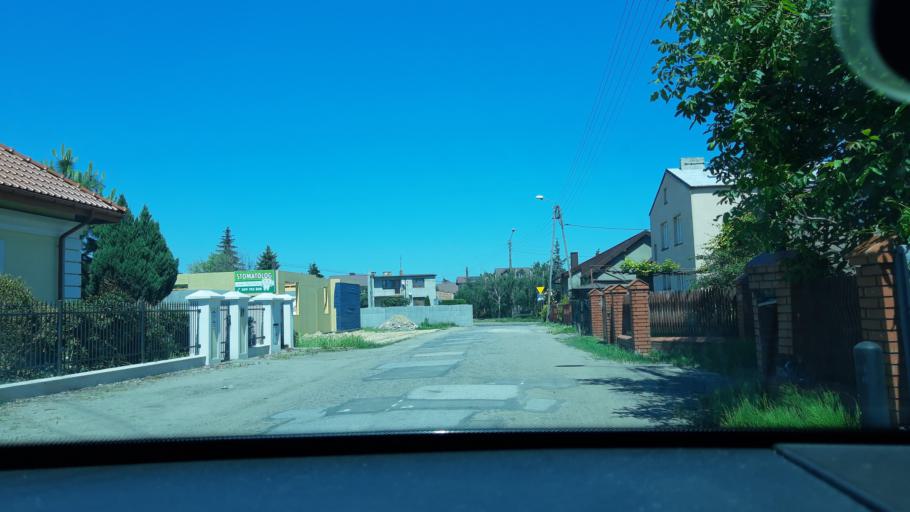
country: PL
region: Lodz Voivodeship
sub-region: Powiat sieradzki
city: Sieradz
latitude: 51.5749
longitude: 18.7442
